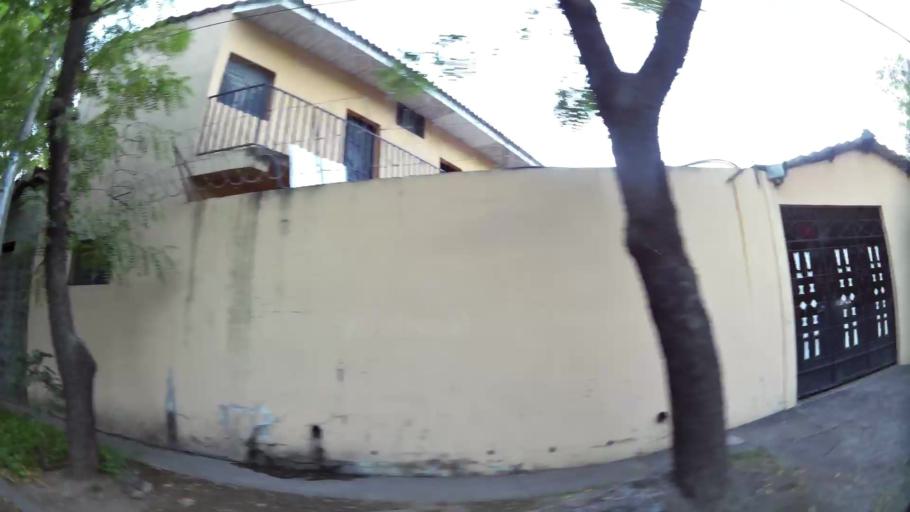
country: SV
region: San Miguel
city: San Miguel
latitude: 13.4820
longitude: -88.1587
